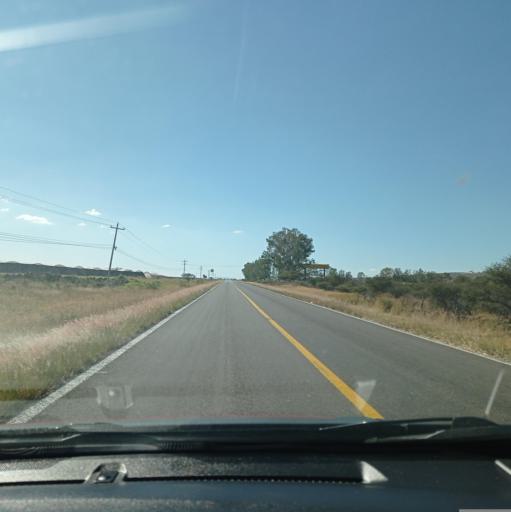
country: MX
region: Jalisco
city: San Miguel el Alto
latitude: 21.0189
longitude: -102.4599
